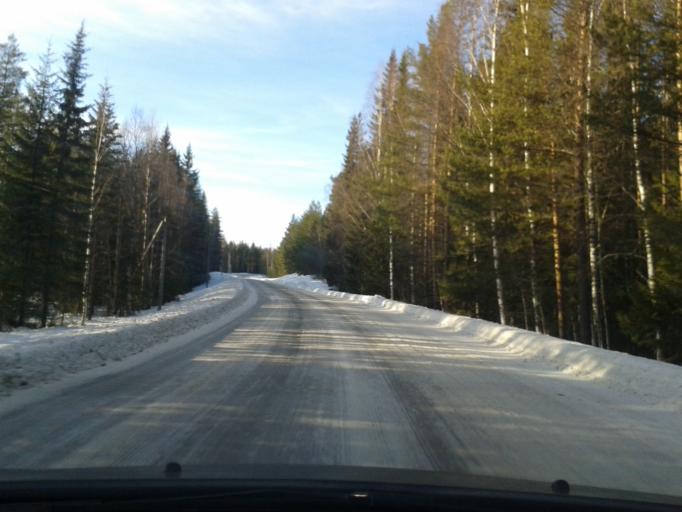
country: SE
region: Vaesternorrland
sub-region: OErnskoeldsviks Kommun
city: Bredbyn
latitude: 63.7424
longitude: 17.7399
